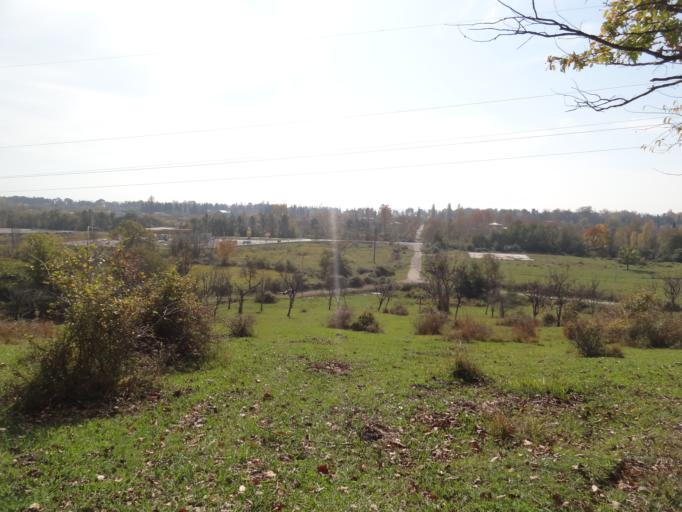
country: GE
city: Gantiadi
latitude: 43.3926
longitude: 40.0349
